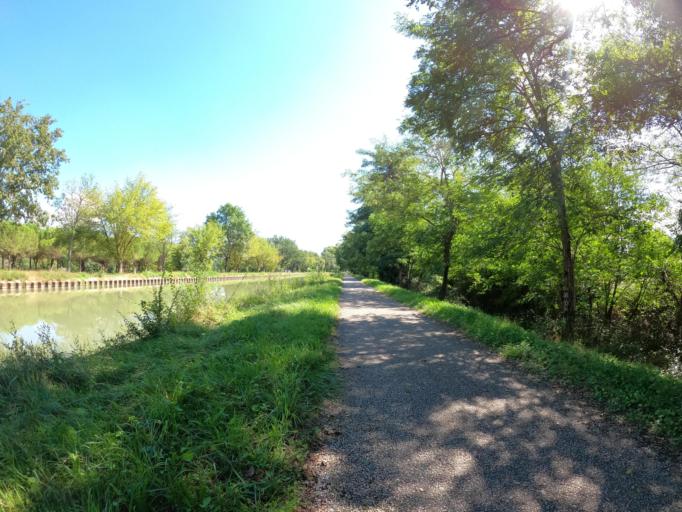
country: FR
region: Midi-Pyrenees
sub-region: Departement du Tarn-et-Garonne
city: Lamagistere
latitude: 44.1259
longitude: 0.8391
